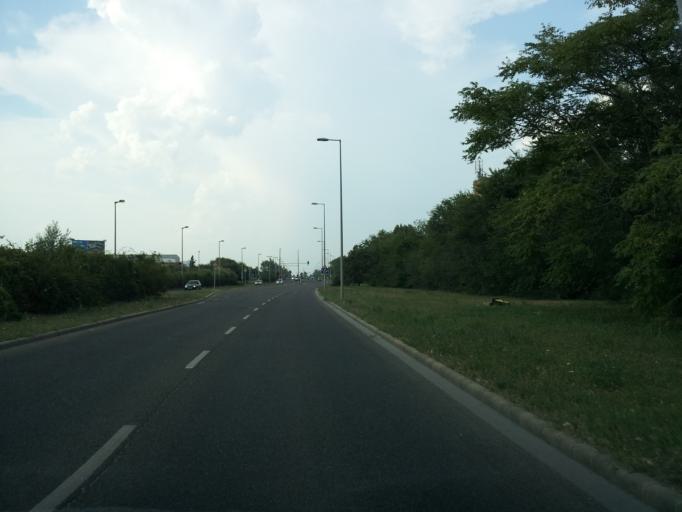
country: HU
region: Budapest
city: Budapest XXII. keruelet
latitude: 47.4462
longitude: 19.0434
